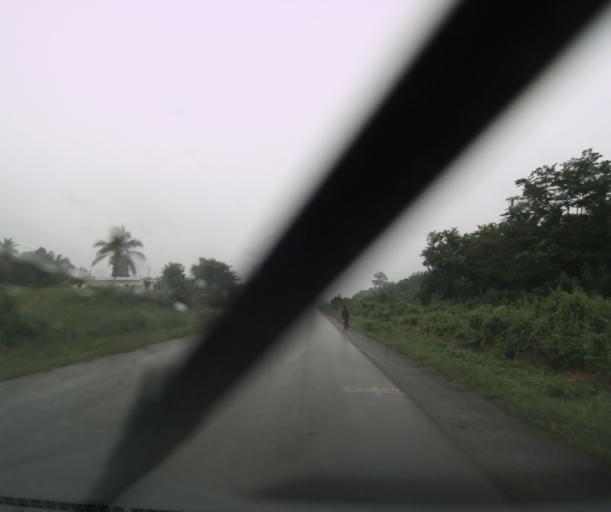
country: CM
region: Littoral
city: Edea
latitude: 3.5908
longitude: 10.1136
